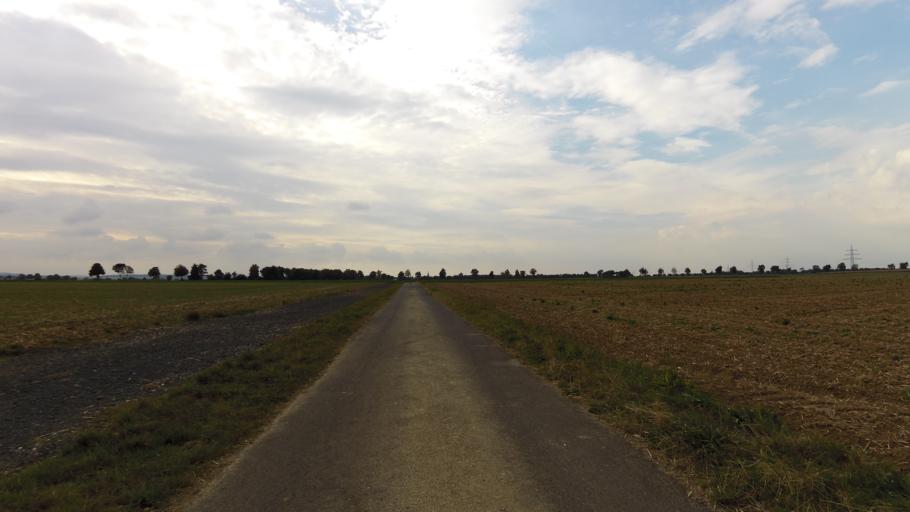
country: DE
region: North Rhine-Westphalia
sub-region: Regierungsbezirk Koln
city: Euskirchen
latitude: 50.6587
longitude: 6.8637
